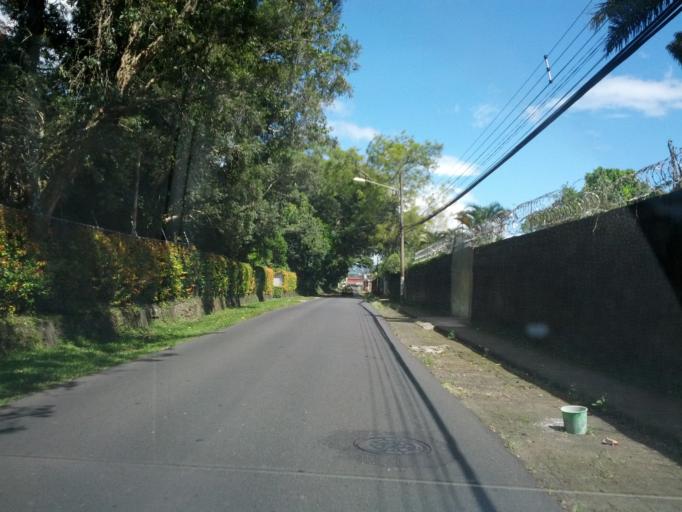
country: CR
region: Alajuela
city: Alajuela
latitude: 10.0214
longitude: -84.2045
